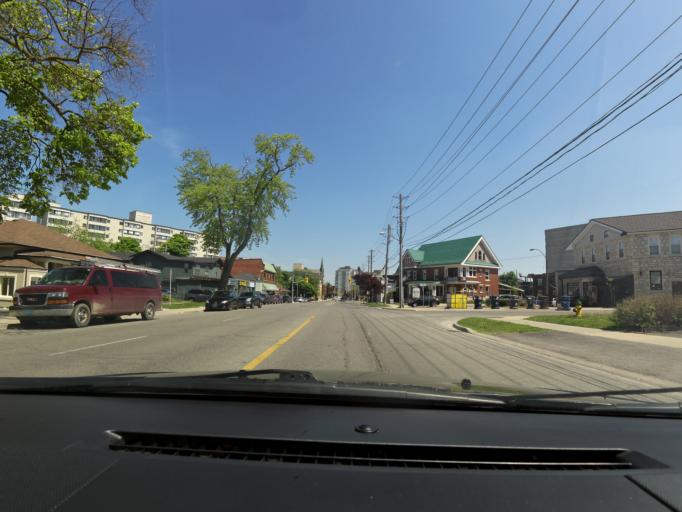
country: CA
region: Ontario
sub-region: Wellington County
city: Guelph
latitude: 43.5484
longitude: -80.2534
